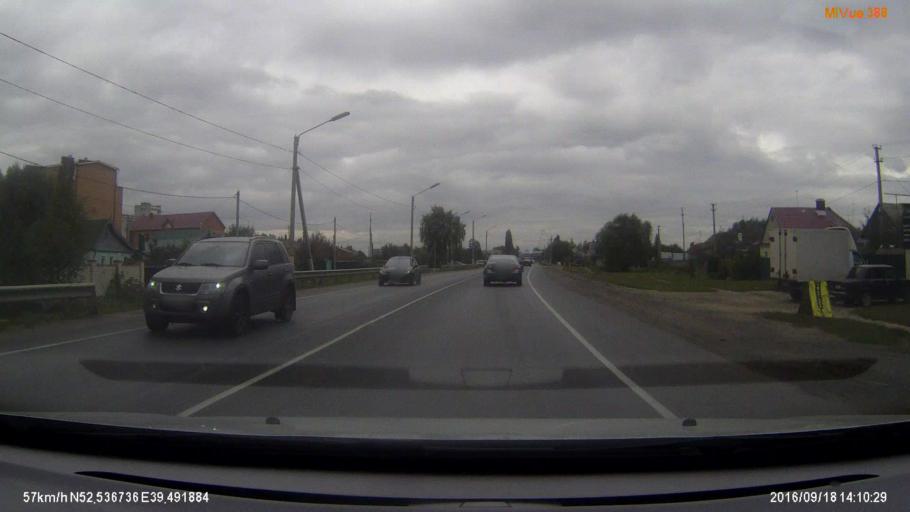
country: RU
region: Lipetsk
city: Syrskoye
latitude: 52.5940
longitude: 39.5181
